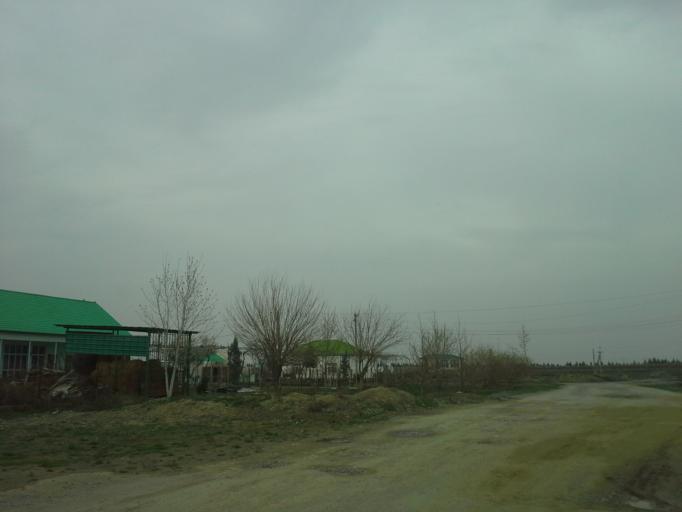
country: TM
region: Ahal
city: Abadan
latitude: 37.9766
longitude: 58.2261
